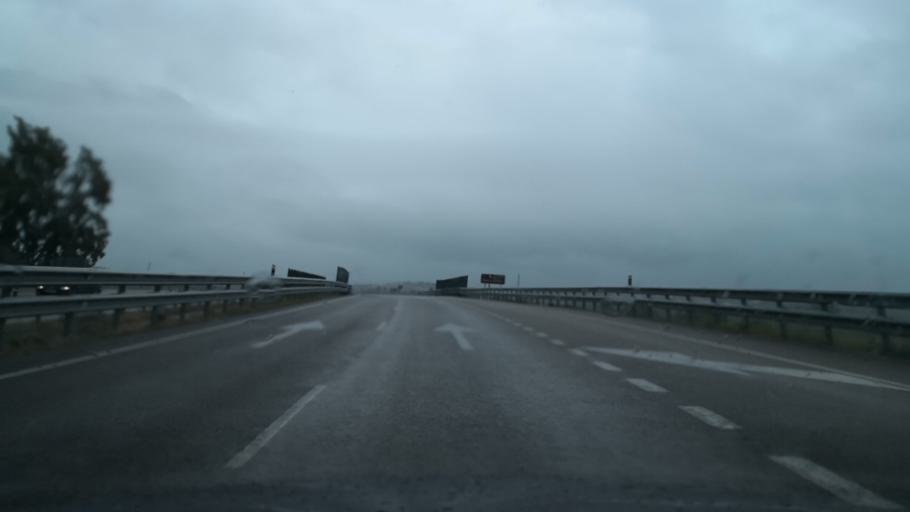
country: ES
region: Extremadura
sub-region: Provincia de Badajoz
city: Badajoz
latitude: 38.9142
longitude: -6.9634
